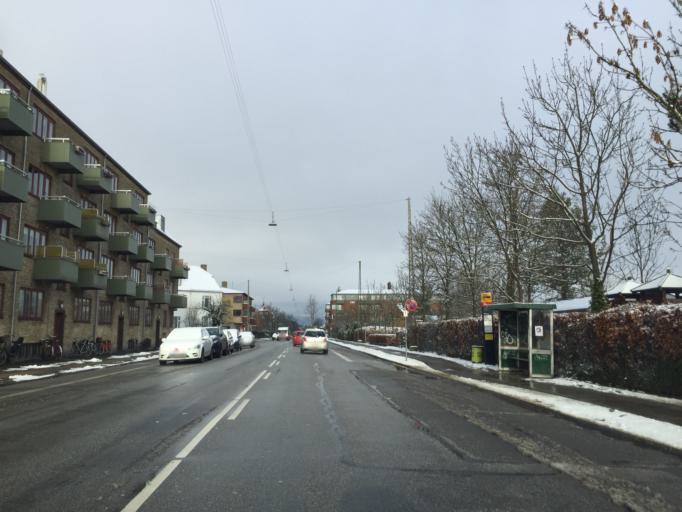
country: DK
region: Capital Region
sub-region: Tarnby Kommune
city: Tarnby
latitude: 55.6527
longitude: 12.6247
